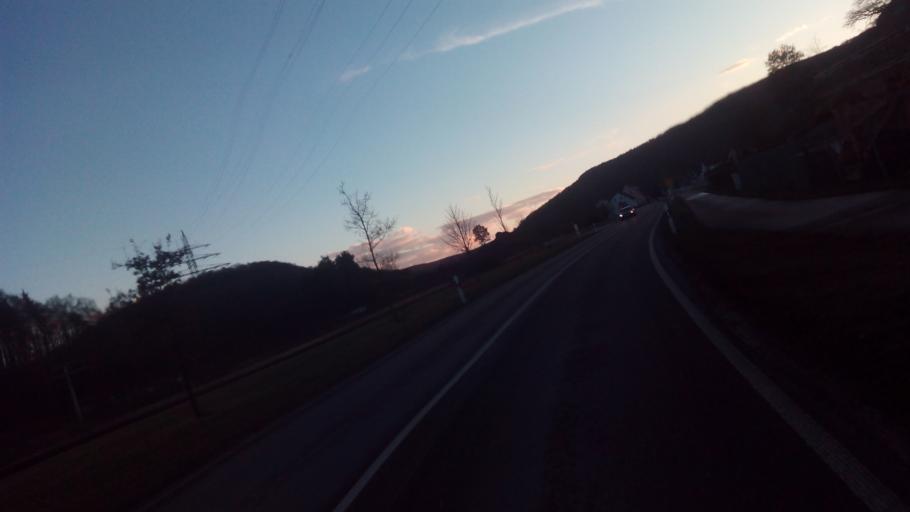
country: DE
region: Baden-Wuerttemberg
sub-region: Tuebingen Region
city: Schelklingen
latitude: 48.3651
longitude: 9.7237
